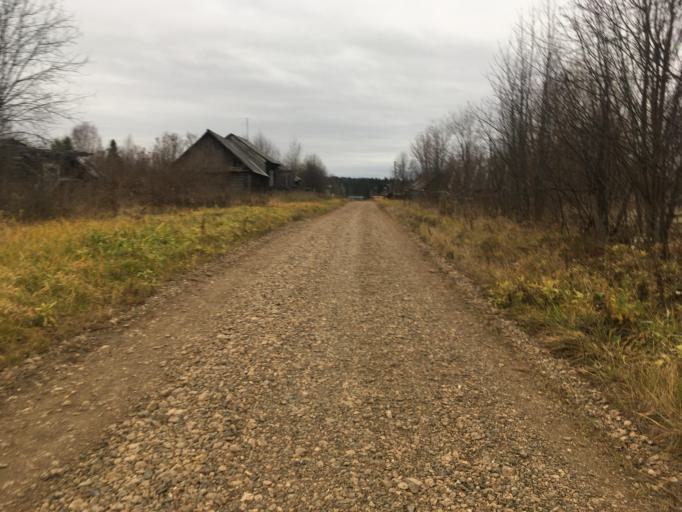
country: RU
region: Perm
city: Komarikhinskiy
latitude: 58.0920
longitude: 57.1121
